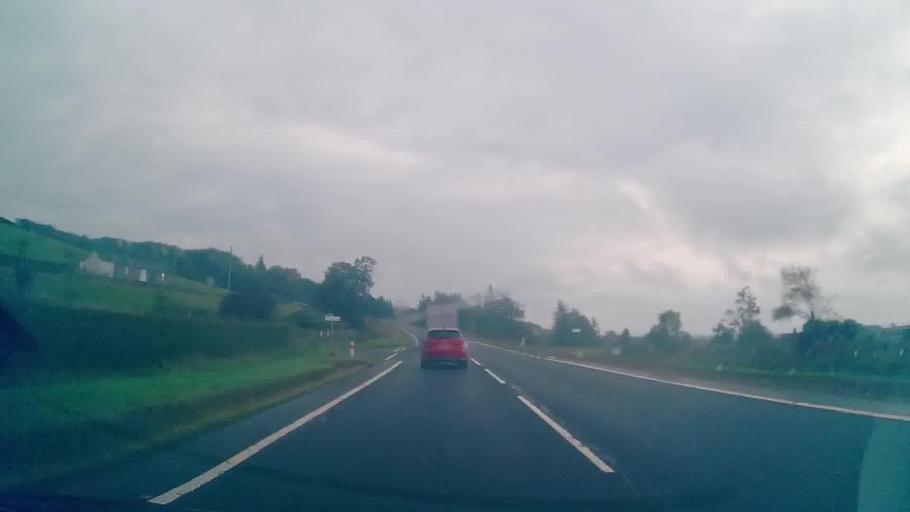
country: GB
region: Scotland
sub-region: Dumfries and Galloway
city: Lochmaben
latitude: 55.0367
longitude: -3.4313
